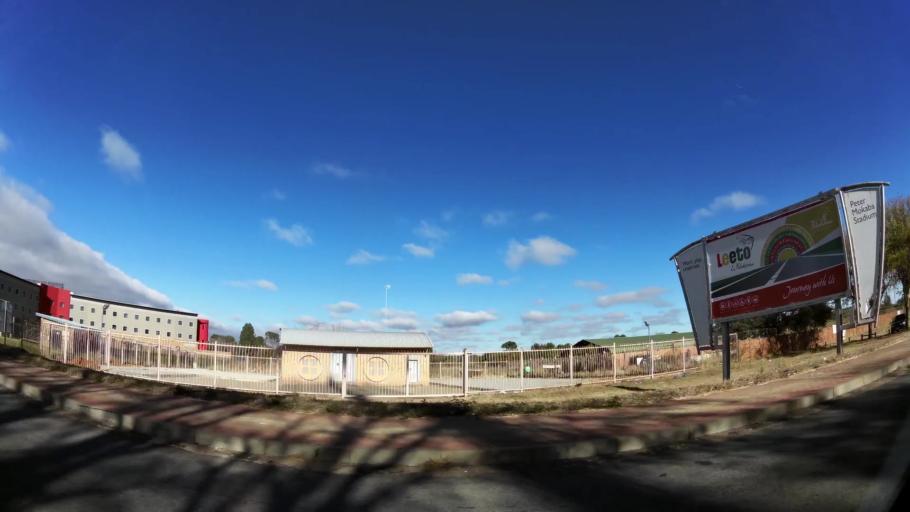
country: ZA
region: Limpopo
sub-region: Capricorn District Municipality
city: Polokwane
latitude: -23.9251
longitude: 29.4636
